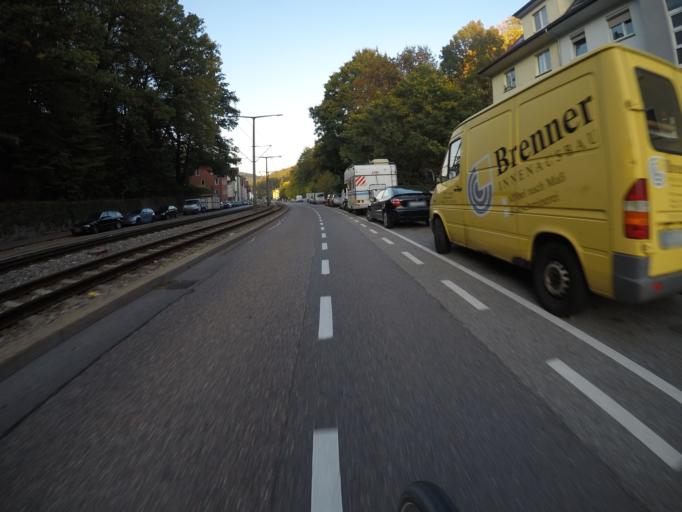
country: DE
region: Baden-Wuerttemberg
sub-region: Regierungsbezirk Stuttgart
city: Stuttgart
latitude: 48.7431
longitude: 9.1332
